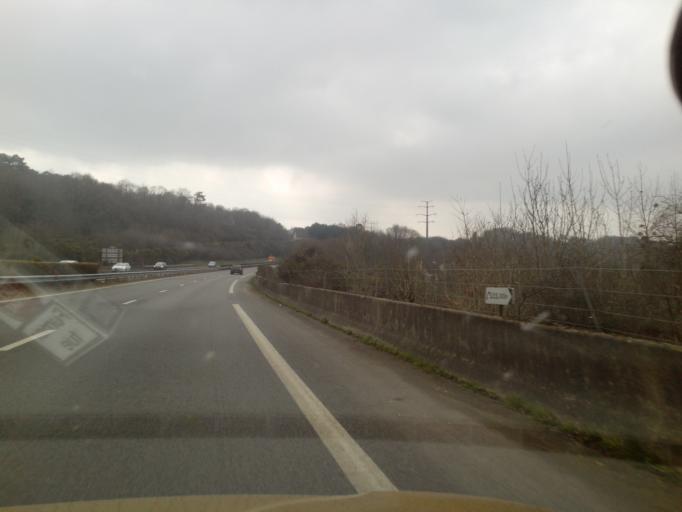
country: FR
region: Brittany
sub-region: Departement du Morbihan
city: Trefflean
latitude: 47.7006
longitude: -2.6212
